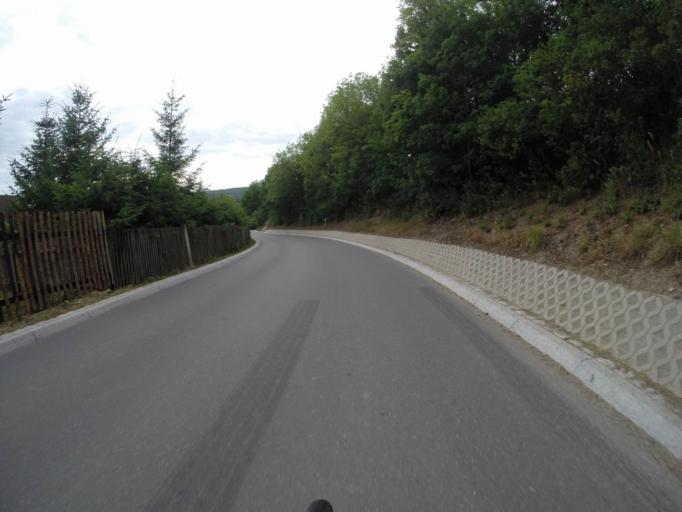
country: DE
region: Thuringia
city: Golmsdorf
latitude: 50.9745
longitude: 11.6732
